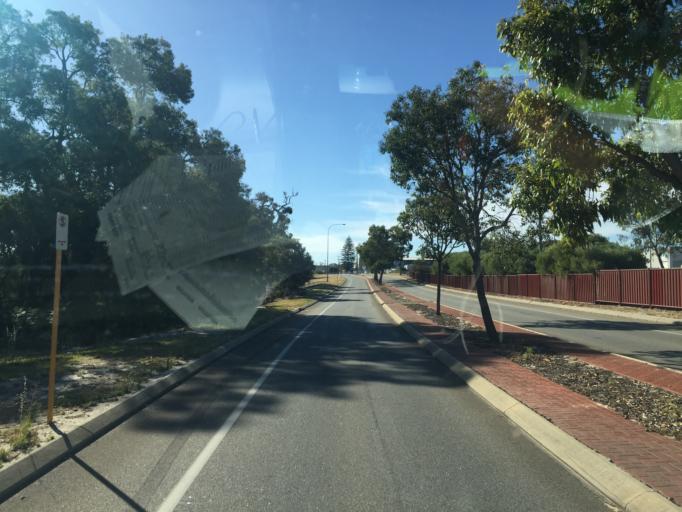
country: AU
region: Western Australia
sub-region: Canning
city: East Cannington
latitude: -32.0028
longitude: 115.9705
